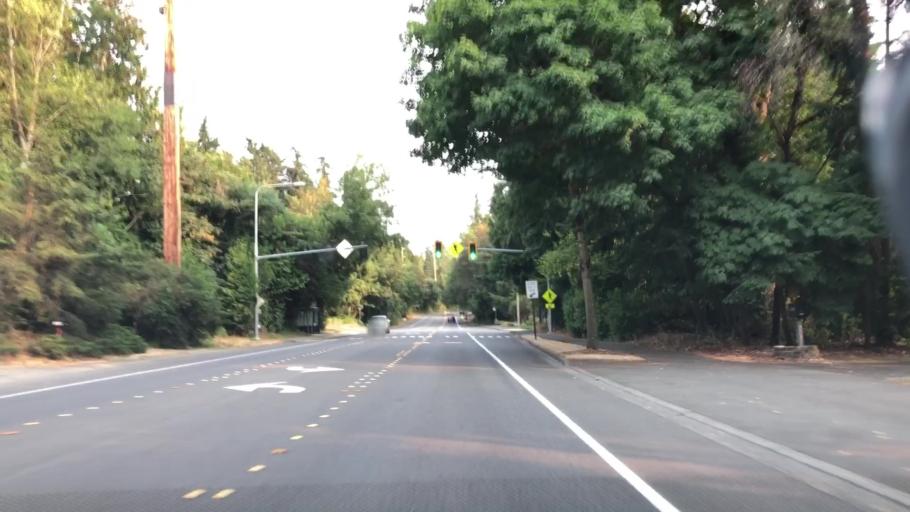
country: US
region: Washington
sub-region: King County
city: Mercer Island
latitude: 47.5626
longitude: -122.2229
